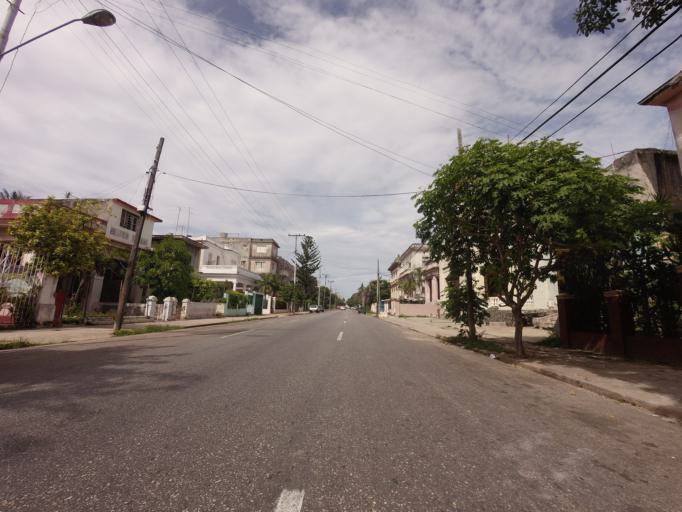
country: CU
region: La Habana
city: Havana
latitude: 23.1308
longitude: -82.4008
